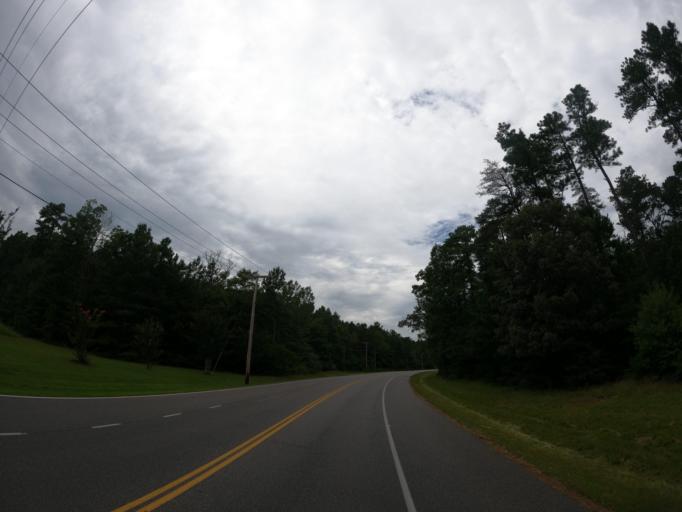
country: US
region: Maryland
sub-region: Saint Mary's County
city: California
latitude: 38.2790
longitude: -76.5503
